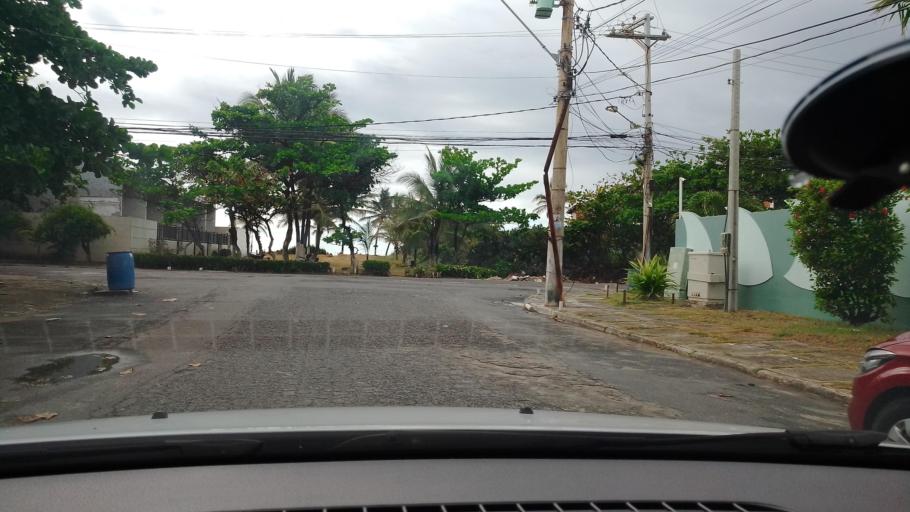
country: BR
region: Bahia
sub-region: Lauro De Freitas
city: Lauro de Freitas
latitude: -12.9329
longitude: -38.3249
